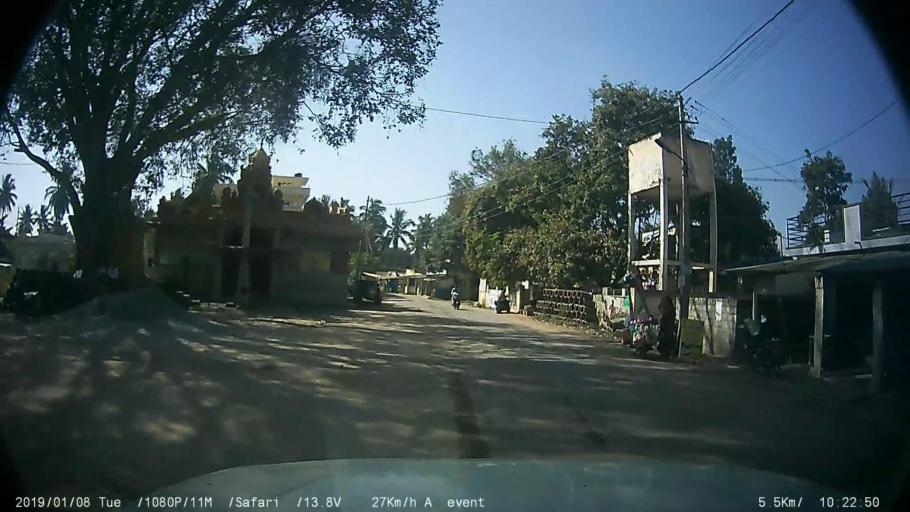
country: IN
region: Karnataka
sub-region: Bangalore Urban
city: Anekal
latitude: 12.8192
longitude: 77.6373
